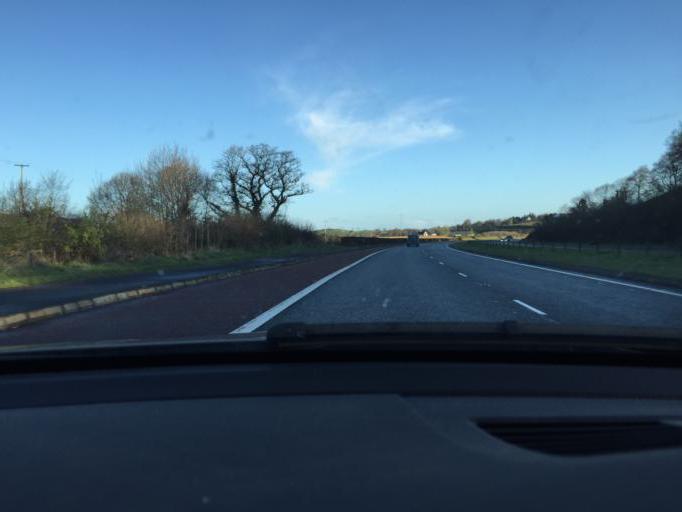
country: GB
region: Northern Ireland
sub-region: Newry and Mourne District
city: Newry
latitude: 54.2439
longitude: -6.3224
